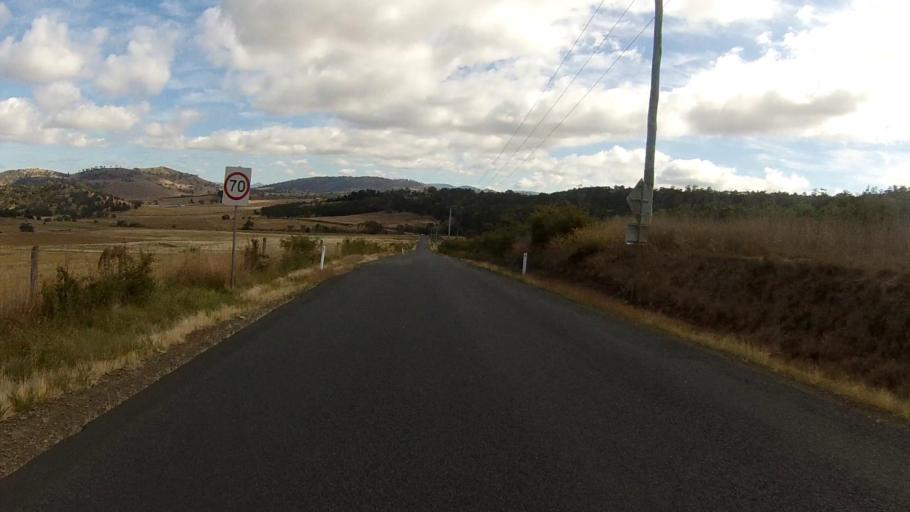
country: AU
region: Tasmania
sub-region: Brighton
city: Old Beach
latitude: -42.7575
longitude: 147.3047
